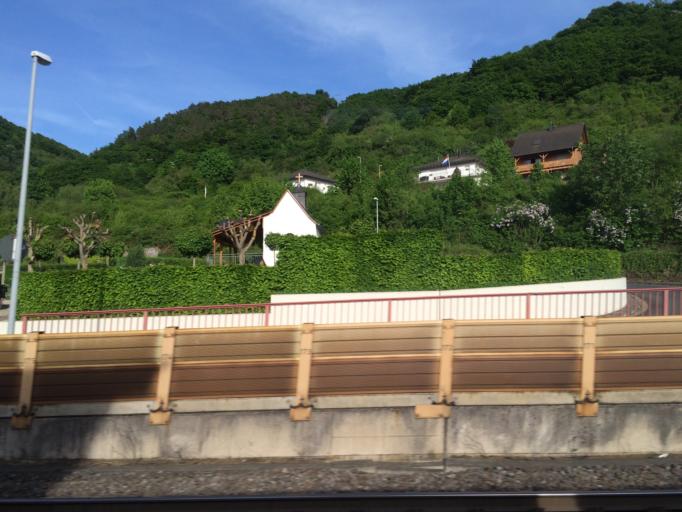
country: DE
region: Rheinland-Pfalz
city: Kestert
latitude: 50.1871
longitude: 7.6490
